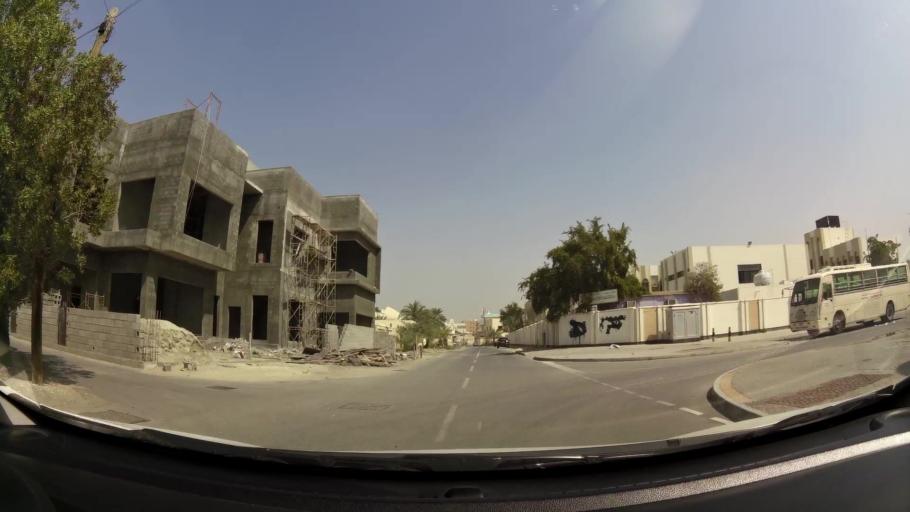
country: BH
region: Manama
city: Jidd Hafs
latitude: 26.2102
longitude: 50.4477
